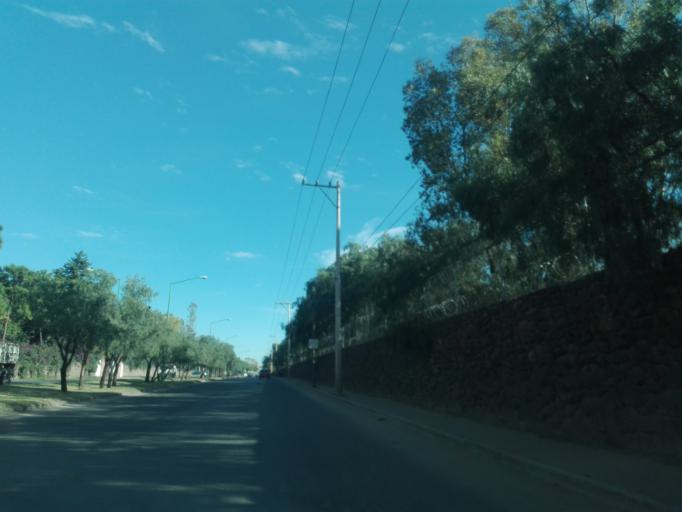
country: MX
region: Guanajuato
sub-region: Leon
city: Fraccionamiento Paraiso Real
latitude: 21.1156
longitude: -101.6079
